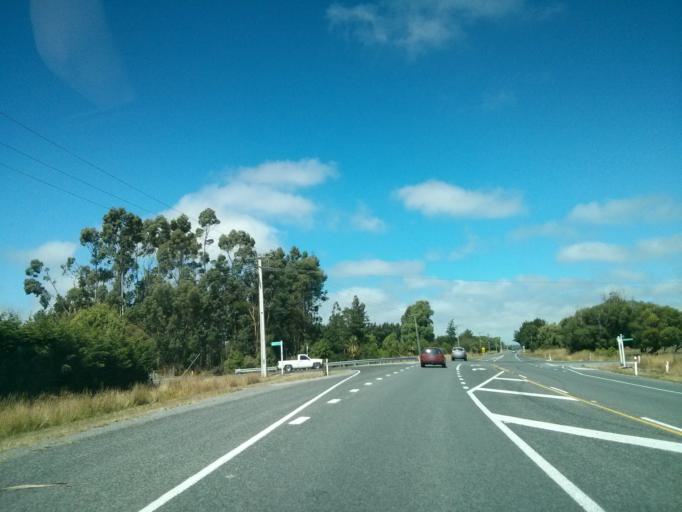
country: NZ
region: Canterbury
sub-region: Waimakariri District
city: Kaiapoi
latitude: -43.3970
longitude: 172.6045
